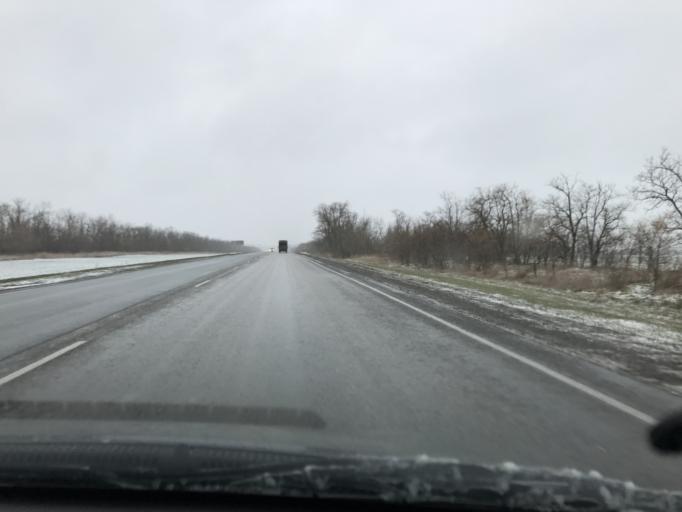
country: RU
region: Rostov
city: Mechetinskaya
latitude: 46.7274
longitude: 40.4815
